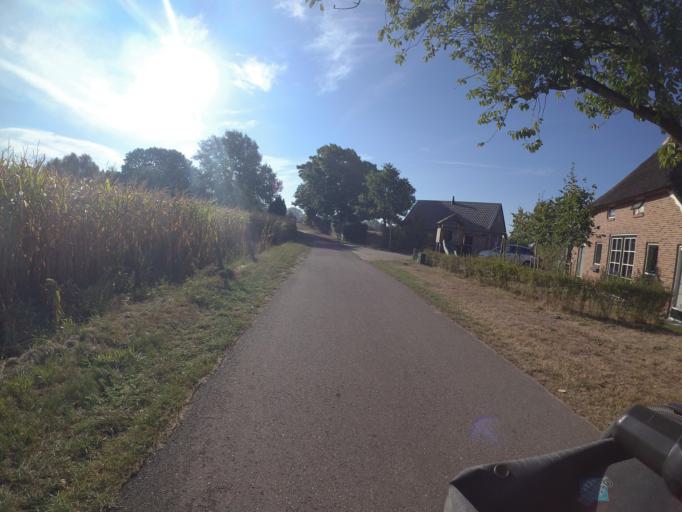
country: NL
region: Overijssel
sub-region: Gemeente Zwartewaterland
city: Hasselt
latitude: 52.5581
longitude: 6.1184
